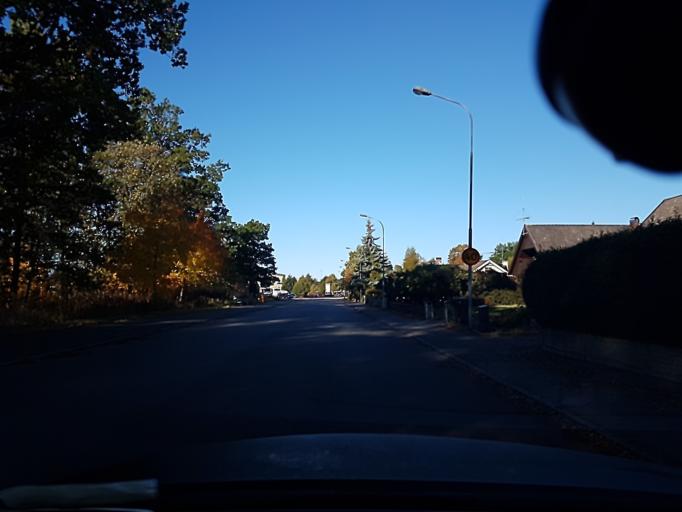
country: SE
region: Kronoberg
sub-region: Vaxjo Kommun
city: Vaexjoe
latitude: 56.8712
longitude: 14.8330
